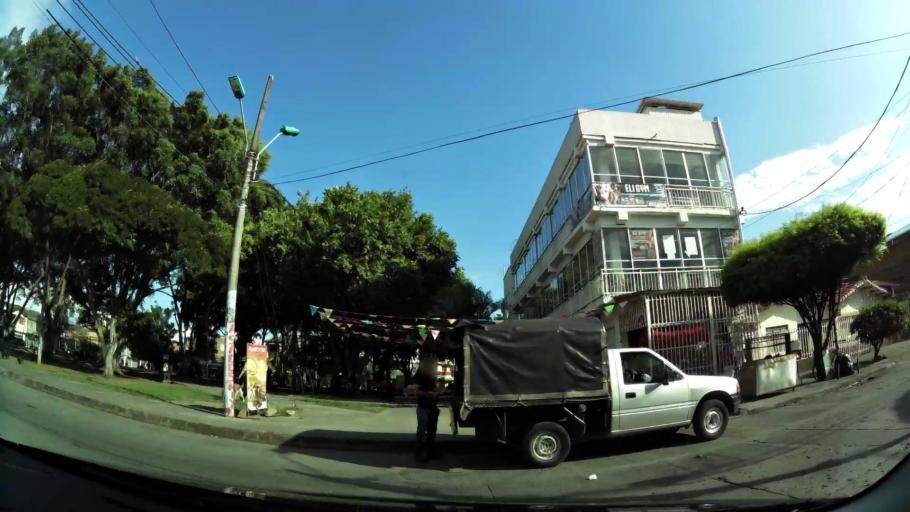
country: CO
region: Valle del Cauca
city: Cali
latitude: 3.4295
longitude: -76.5250
